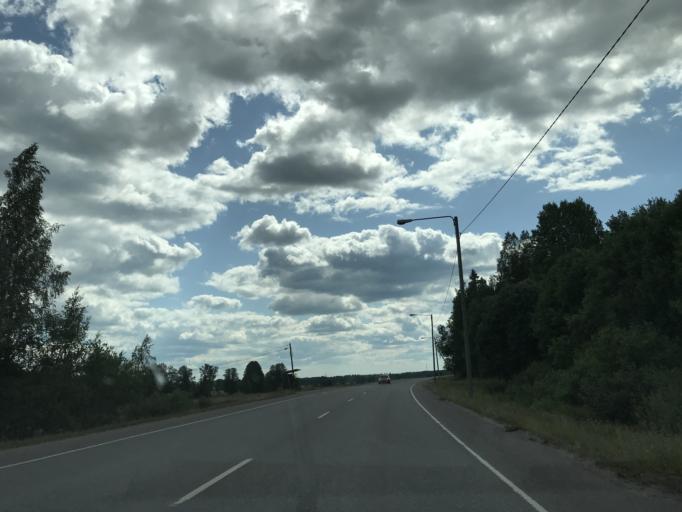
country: FI
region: Uusimaa
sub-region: Helsinki
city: Maentsaelae
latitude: 60.6641
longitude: 25.3500
